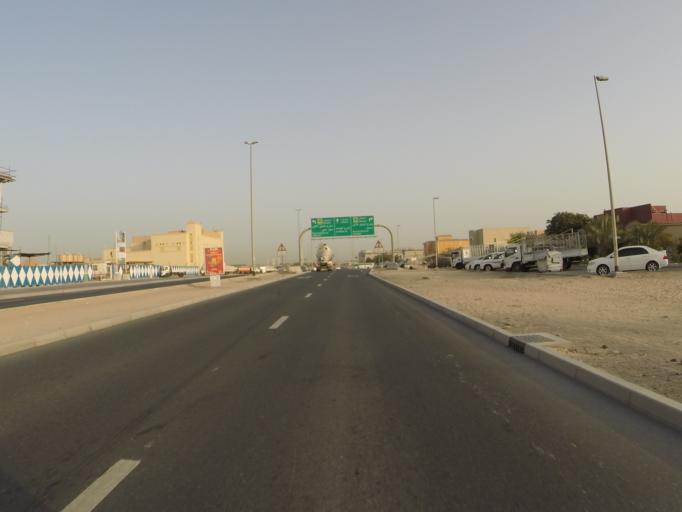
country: AE
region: Dubai
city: Dubai
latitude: 25.1629
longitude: 55.2486
